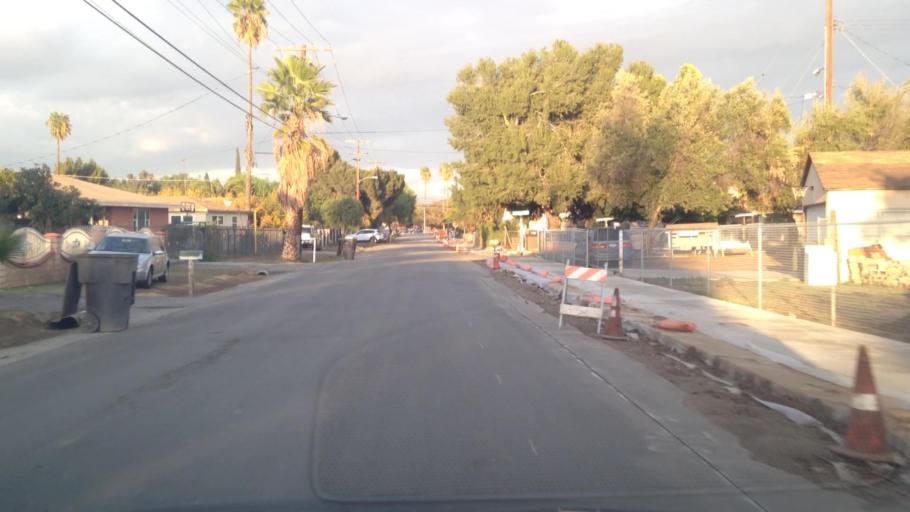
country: US
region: California
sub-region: Riverside County
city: Pedley
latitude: 33.9212
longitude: -117.4864
